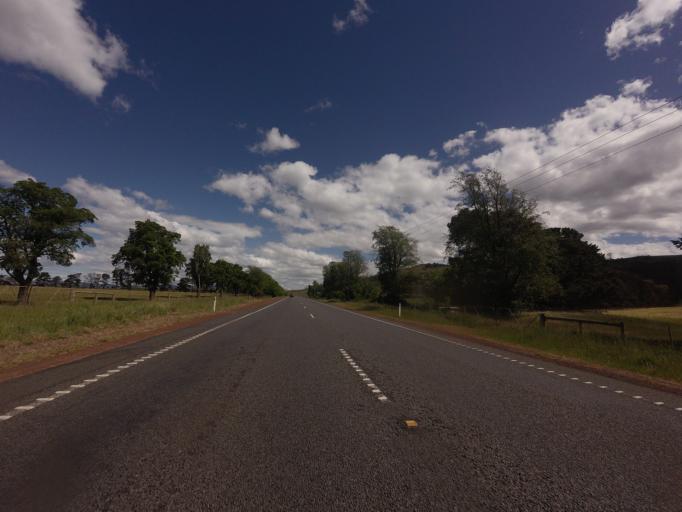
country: AU
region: Tasmania
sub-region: Northern Midlands
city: Evandale
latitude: -42.0417
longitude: 147.4829
